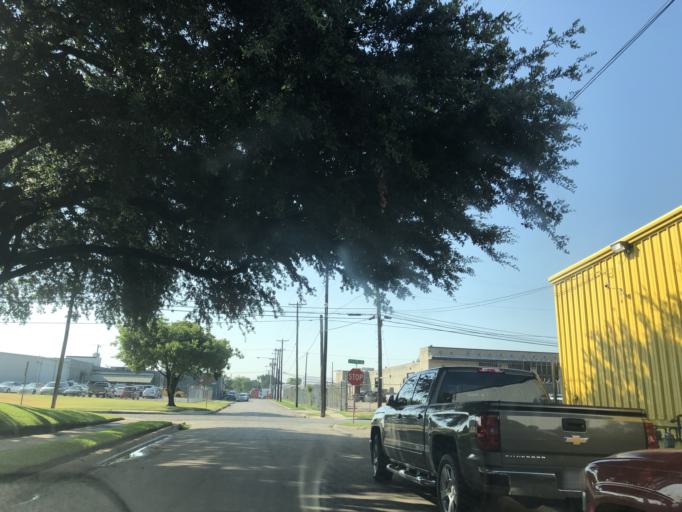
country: US
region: Texas
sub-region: Dallas County
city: Dallas
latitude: 32.7720
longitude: -96.7772
